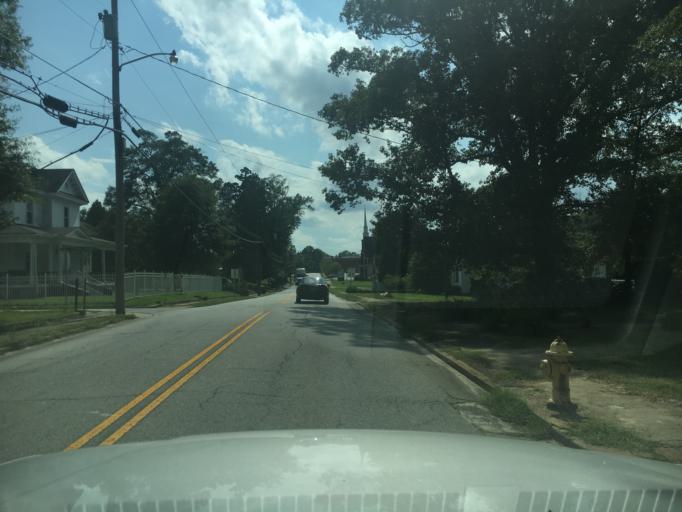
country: US
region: South Carolina
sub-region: Anderson County
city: Belton
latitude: 34.5247
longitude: -82.4901
